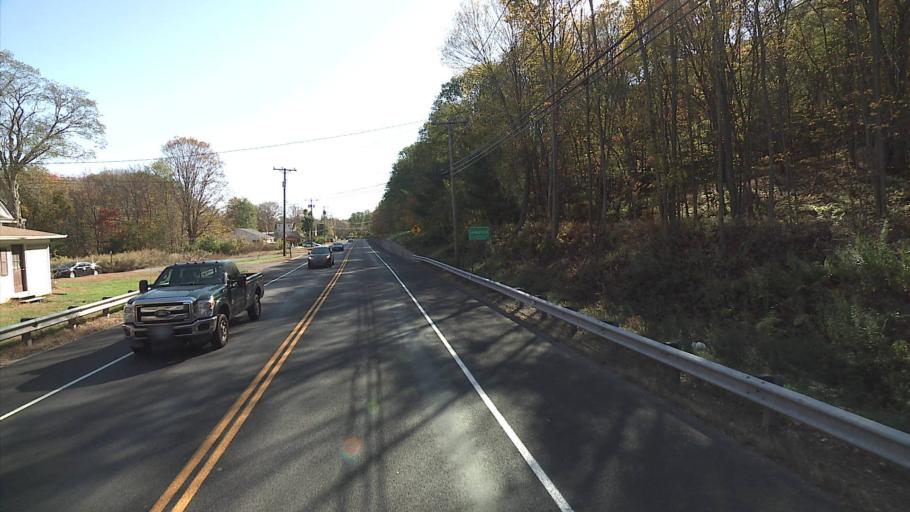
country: US
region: Connecticut
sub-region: Tolland County
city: Coventry Lake
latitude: 41.7405
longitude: -72.3783
